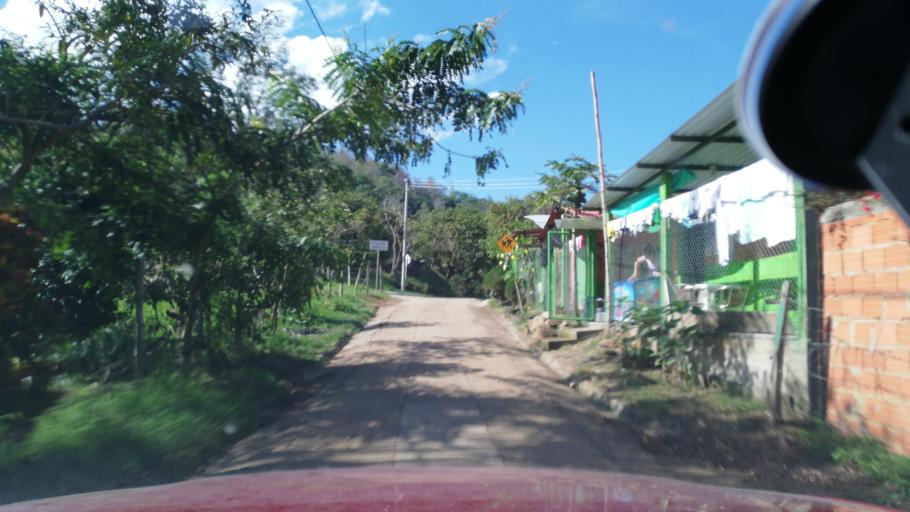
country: CO
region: Cundinamarca
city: Quipile
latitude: 4.7707
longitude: -74.6133
